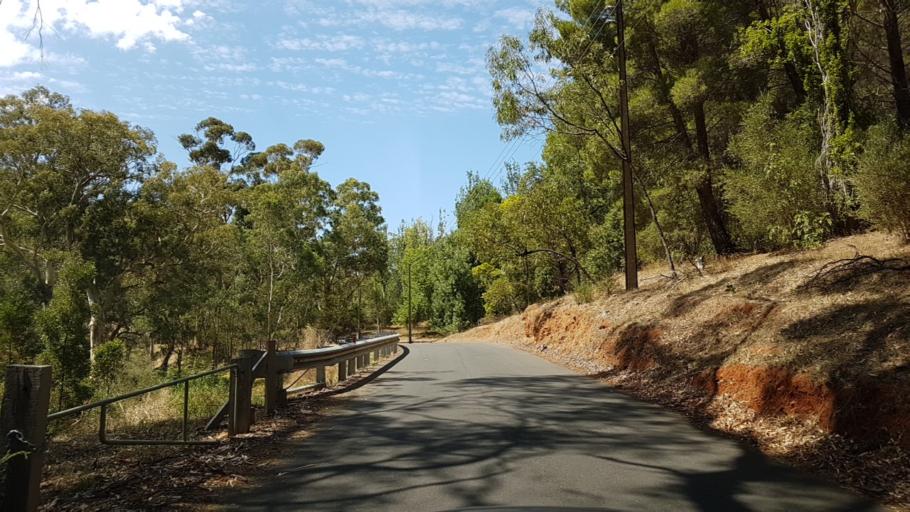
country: AU
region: South Australia
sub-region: Mitcham
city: Mitcham
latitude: -34.9887
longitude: 138.6399
